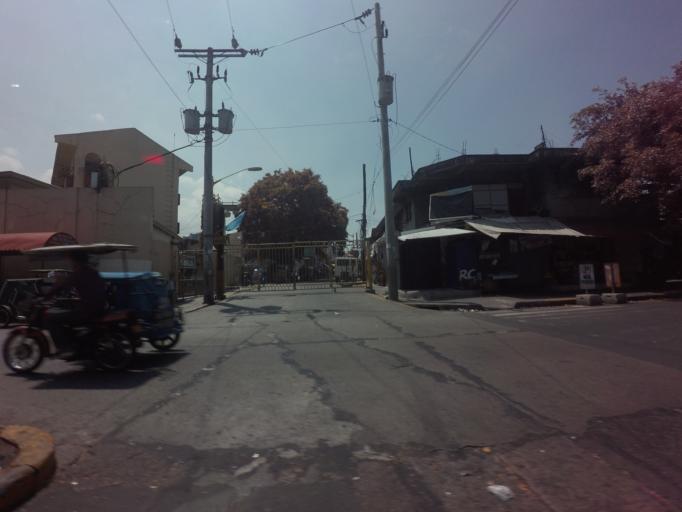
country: PH
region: Metro Manila
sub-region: Makati City
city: Makati City
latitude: 14.5692
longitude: 121.0063
